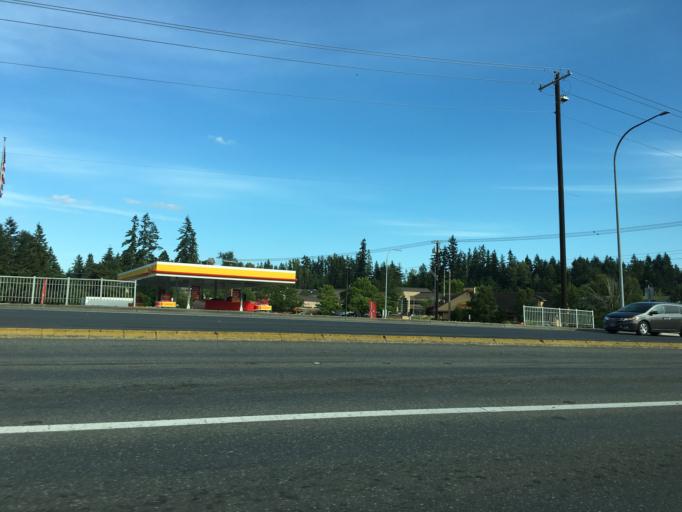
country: US
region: Washington
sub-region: King County
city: Bothell
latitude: 47.7921
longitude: -122.2162
